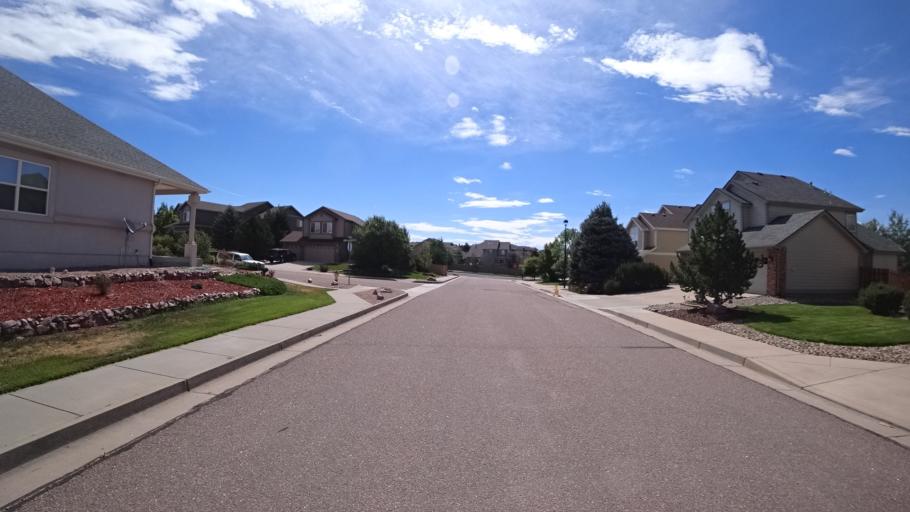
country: US
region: Colorado
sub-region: El Paso County
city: Gleneagle
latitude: 39.0311
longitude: -104.8177
